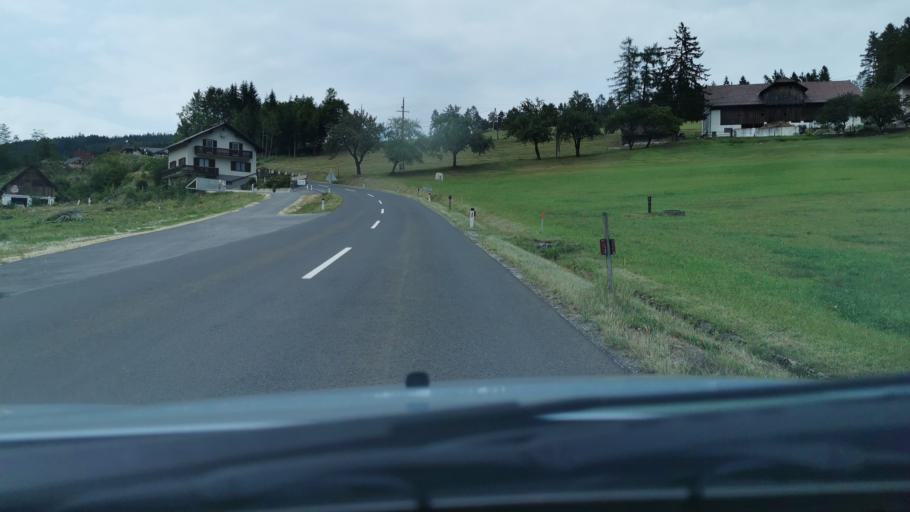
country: AT
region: Styria
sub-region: Politischer Bezirk Weiz
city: Fischbach
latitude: 47.3948
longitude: 15.6683
